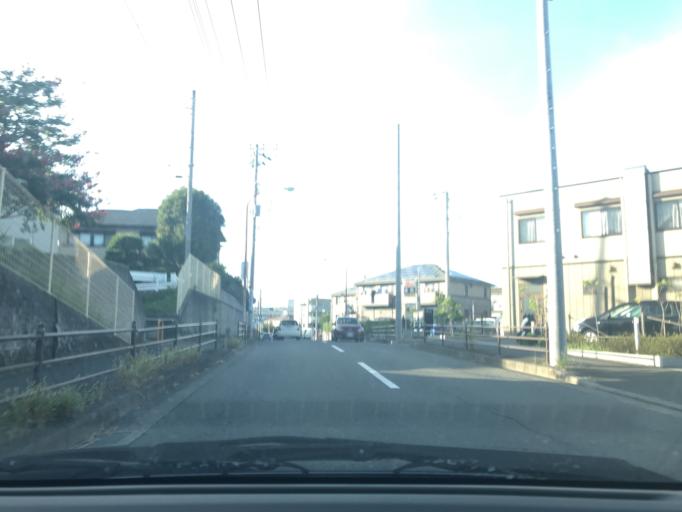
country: JP
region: Kanagawa
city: Fujisawa
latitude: 35.3421
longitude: 139.4627
